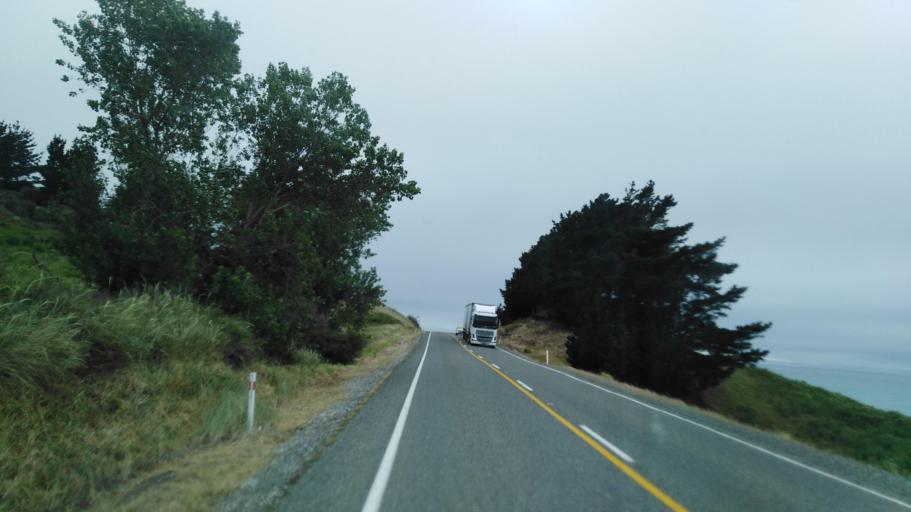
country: NZ
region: Marlborough
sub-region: Marlborough District
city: Blenheim
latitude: -41.9138
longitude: 174.1004
